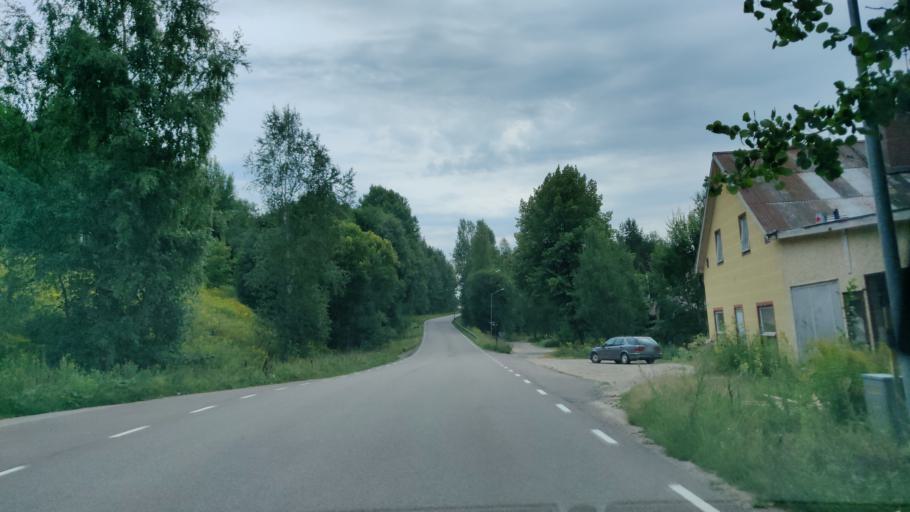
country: SE
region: Vaermland
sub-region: Munkfors Kommun
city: Munkfors
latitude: 59.8345
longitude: 13.5365
